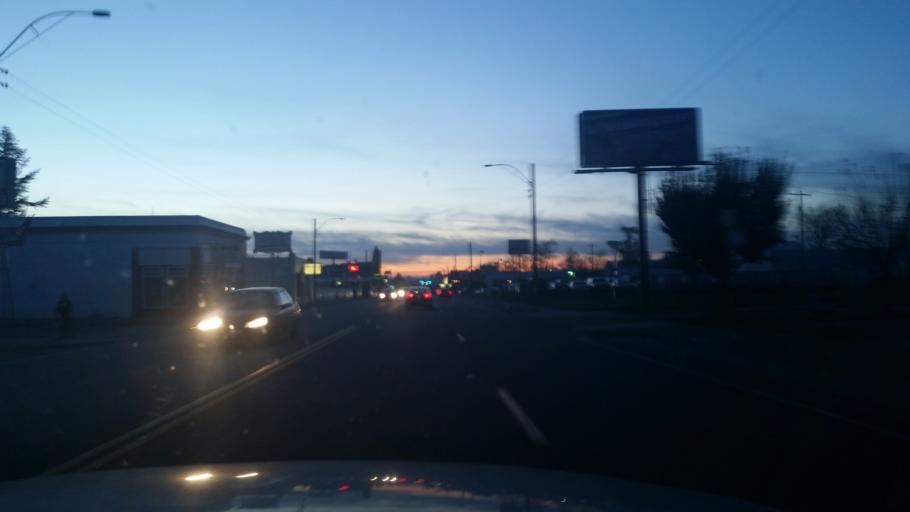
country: US
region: Washington
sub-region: Spokane County
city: Spokane
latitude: 47.6573
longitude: -117.3702
